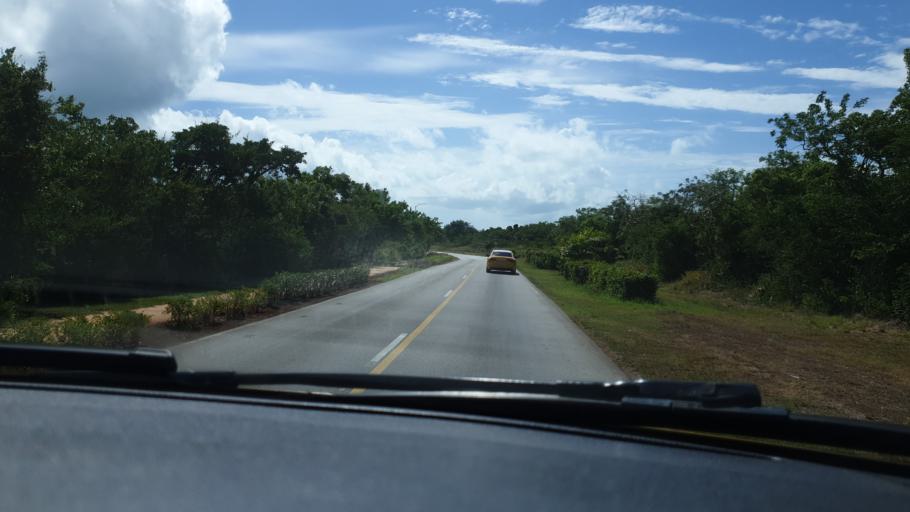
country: CU
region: Sancti Spiritus
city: Yaguajay
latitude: 22.6560
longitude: -79.0345
